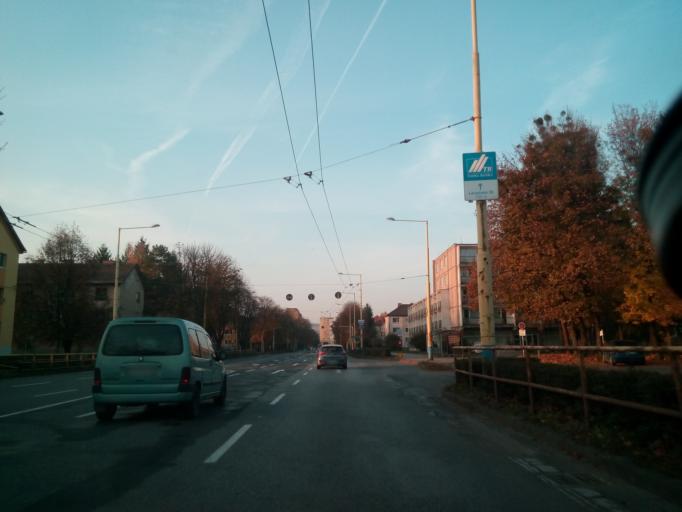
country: SK
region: Presovsky
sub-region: Okres Presov
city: Presov
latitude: 48.9950
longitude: 21.2297
